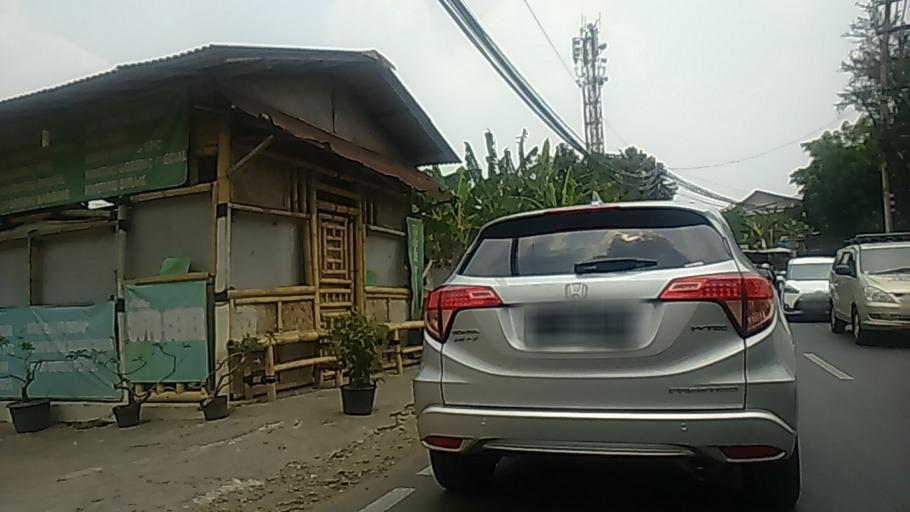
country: ID
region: West Java
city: Pamulang
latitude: -6.2998
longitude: 106.7769
